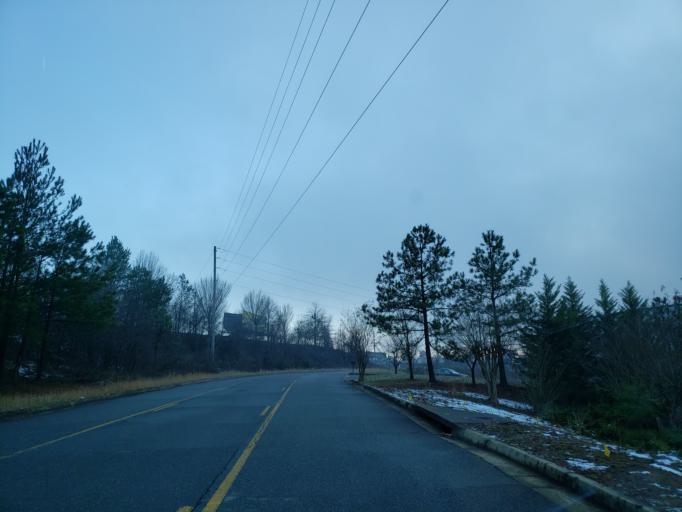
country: US
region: Georgia
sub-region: Cobb County
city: Marietta
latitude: 33.9856
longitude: -84.5644
